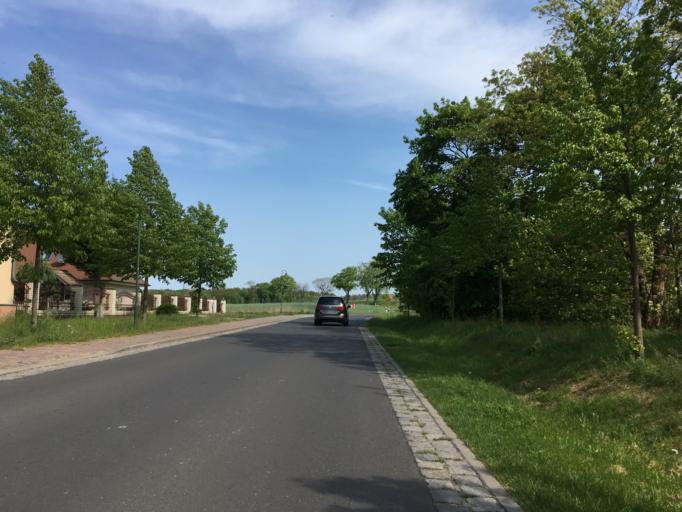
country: DE
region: Brandenburg
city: Werneuchen
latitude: 52.6067
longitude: 13.7570
